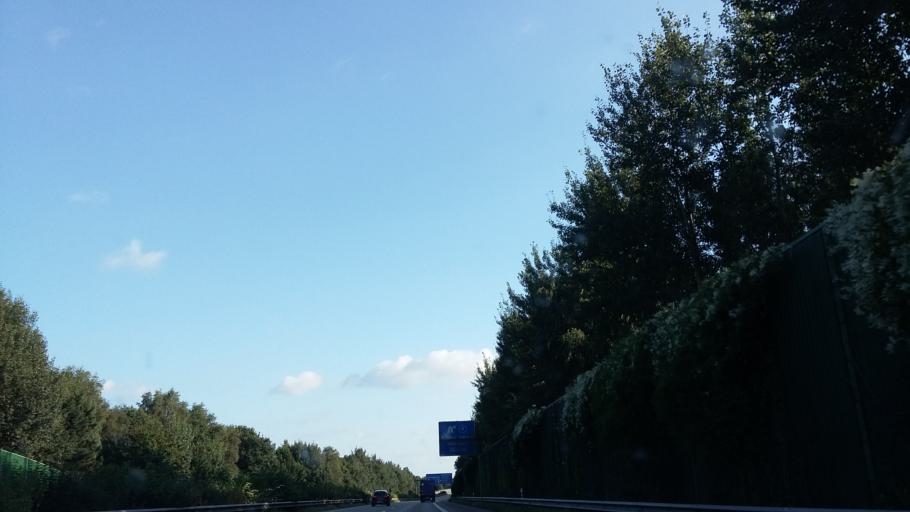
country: DE
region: Lower Saxony
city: Schiffdorf
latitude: 53.5078
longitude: 8.6289
